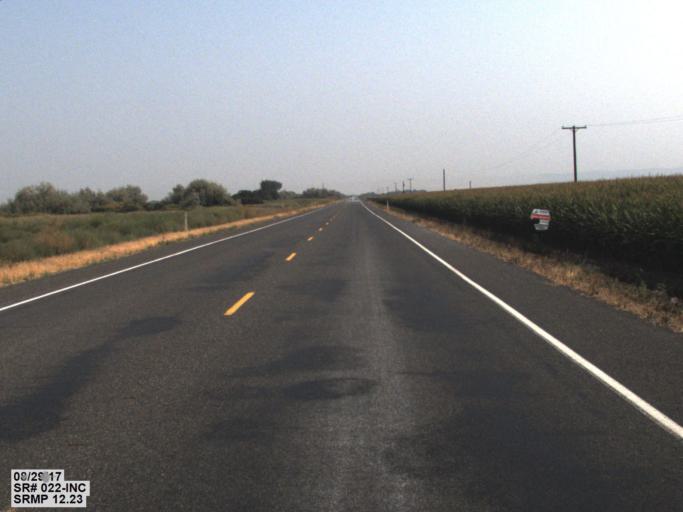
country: US
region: Washington
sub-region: Yakima County
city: Granger
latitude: 46.2954
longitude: -120.1876
